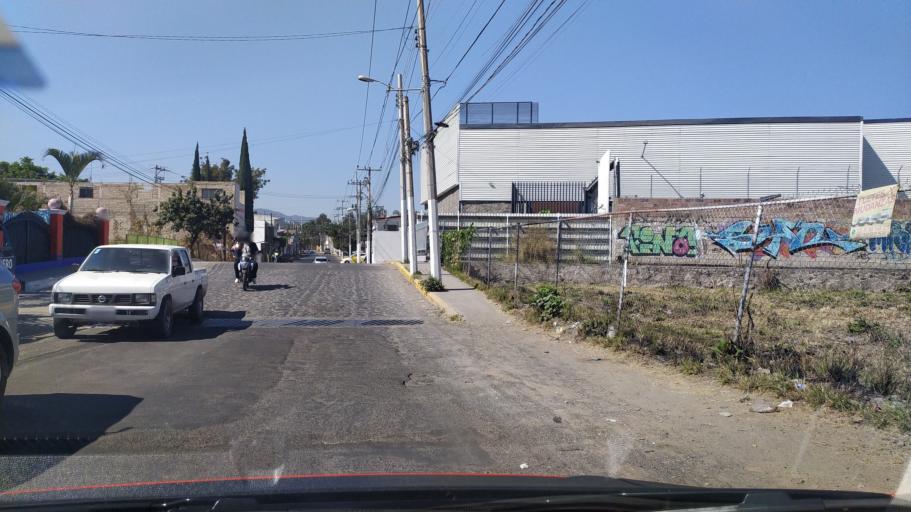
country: MX
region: Jalisco
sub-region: Tlajomulco de Zuniga
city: Palomar
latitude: 20.6290
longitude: -103.4370
